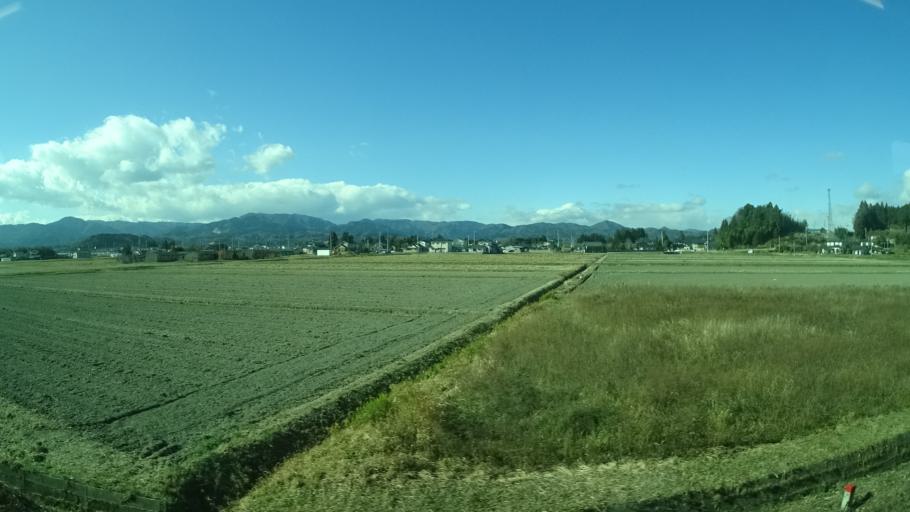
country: JP
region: Fukushima
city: Namie
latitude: 37.6535
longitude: 140.9669
